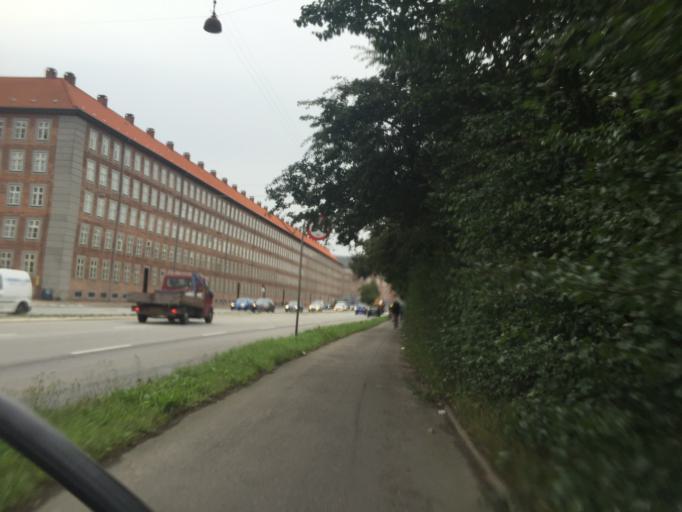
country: DK
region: Capital Region
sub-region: Frederiksberg Kommune
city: Frederiksberg
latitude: 55.6902
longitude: 12.5382
